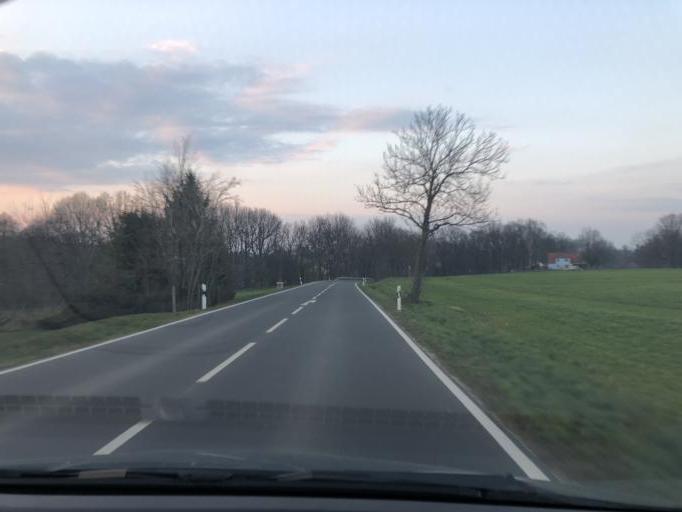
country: DE
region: Saxony
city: Elstra
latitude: 51.2307
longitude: 14.1297
